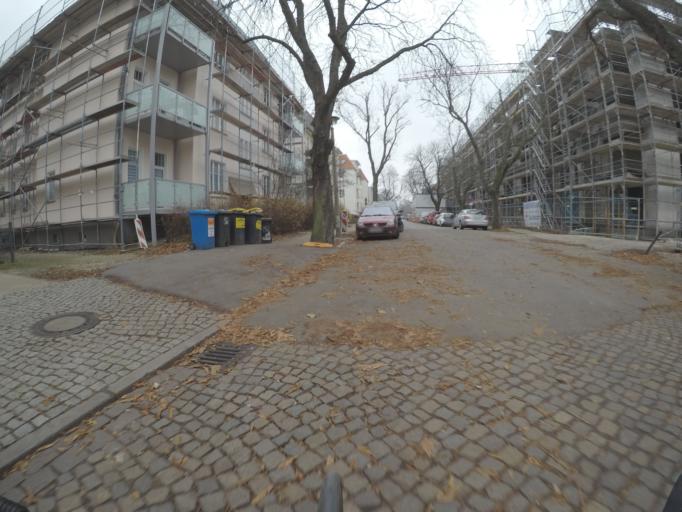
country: DE
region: Berlin
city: Oberschoneweide
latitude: 52.4591
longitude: 13.5346
